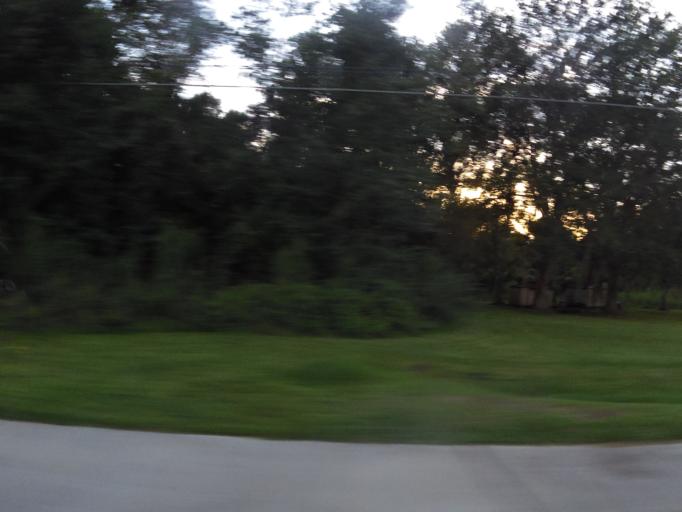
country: US
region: Georgia
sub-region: Camden County
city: Woodbine
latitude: 30.9511
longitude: -81.7203
